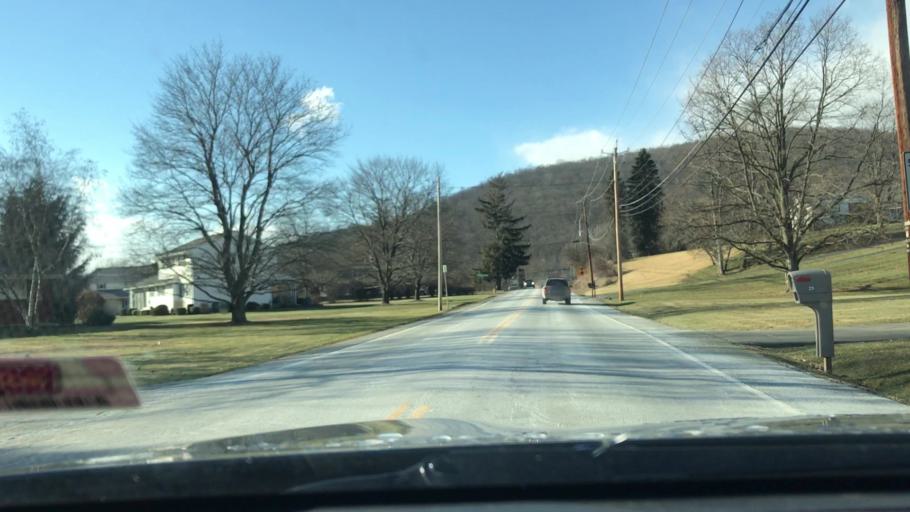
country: US
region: New York
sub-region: Chemung County
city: Big Flats
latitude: 42.1600
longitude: -76.9210
